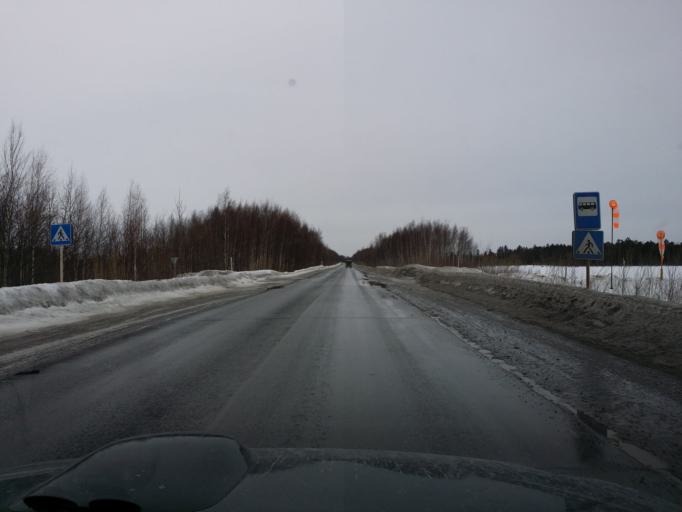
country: RU
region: Tomsk
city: Strezhevoy
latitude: 60.7417
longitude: 77.5323
